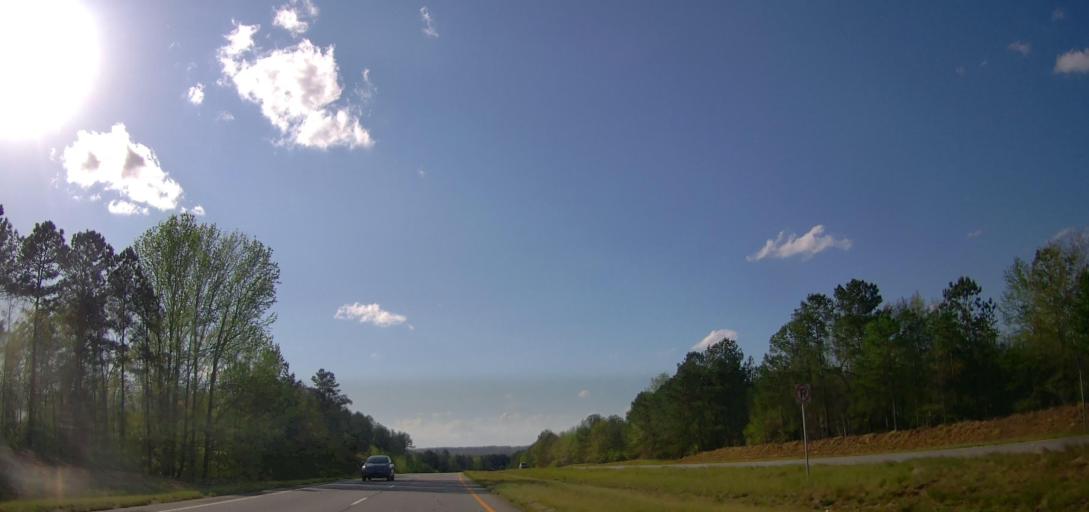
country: US
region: Georgia
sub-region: Baldwin County
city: Hardwick
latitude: 33.0245
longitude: -83.2379
